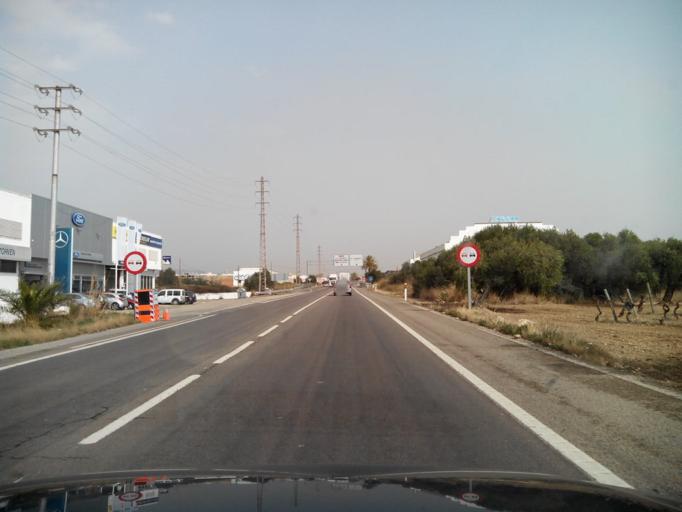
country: ES
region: Catalonia
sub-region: Provincia de Tarragona
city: El Vendrell
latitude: 41.2033
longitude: 1.5305
